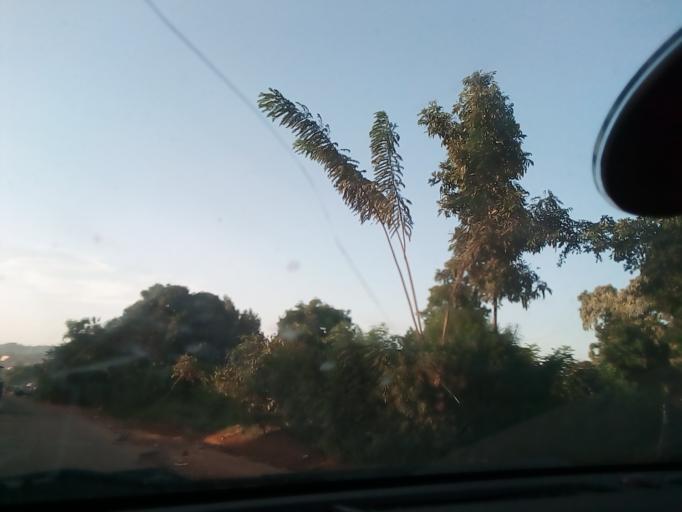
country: UG
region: Central Region
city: Masaka
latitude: -0.3270
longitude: 31.7610
